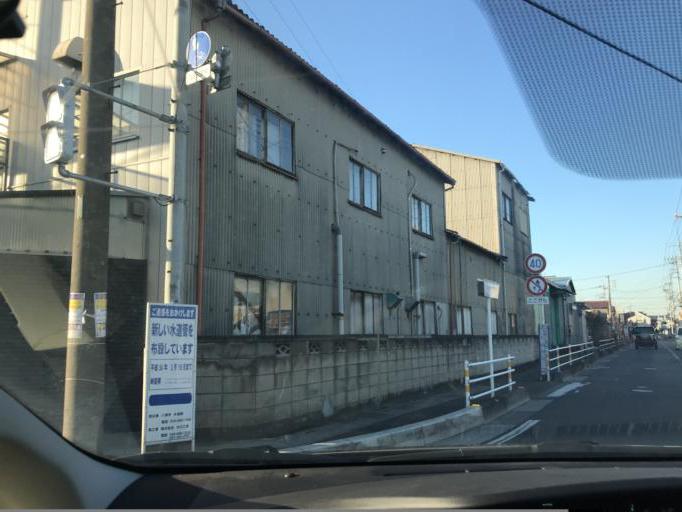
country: JP
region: Saitama
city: Yashio-shi
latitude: 35.8334
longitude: 139.8364
